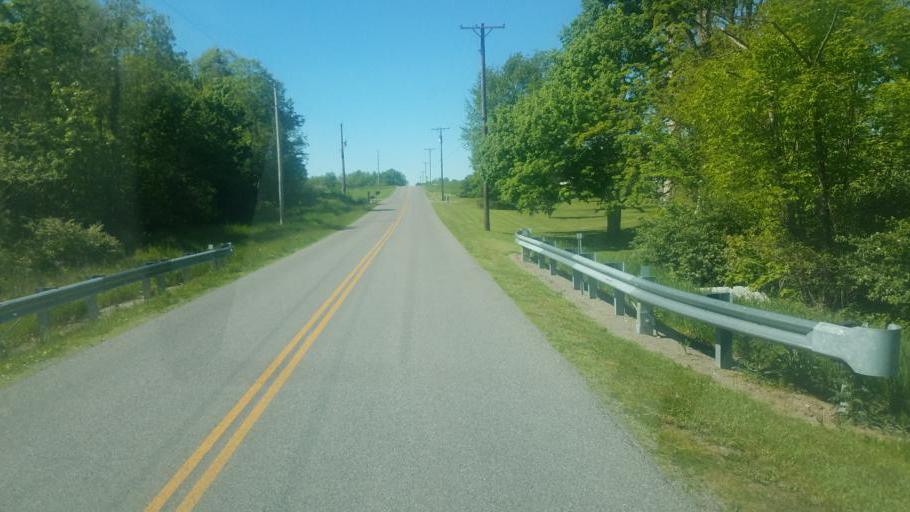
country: US
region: Ohio
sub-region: Logan County
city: Northwood
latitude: 40.4207
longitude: -83.7540
